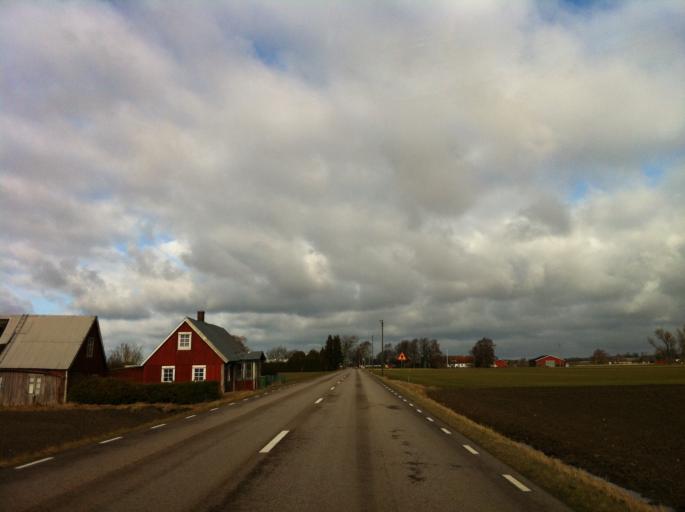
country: SE
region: Skane
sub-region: Bjuvs Kommun
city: Bjuv
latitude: 56.0979
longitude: 12.8919
